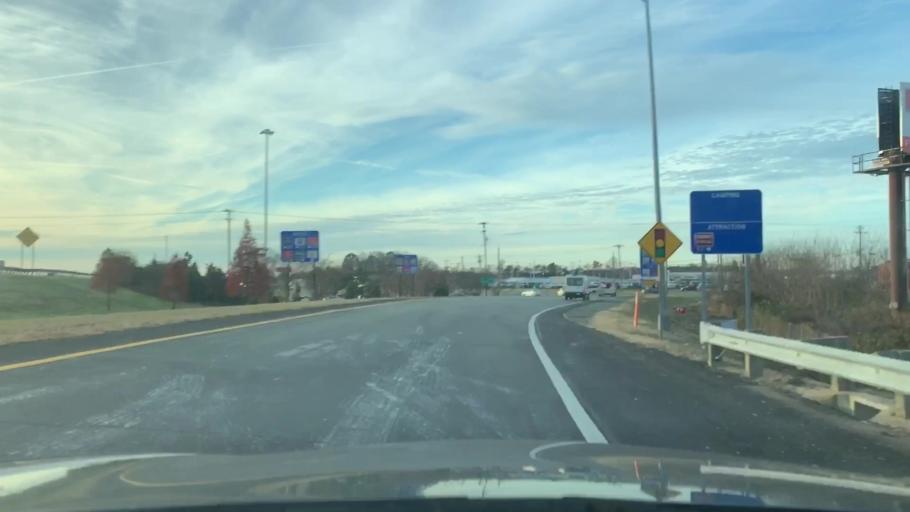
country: US
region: North Carolina
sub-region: Alamance County
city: Graham
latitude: 36.0640
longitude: -79.4292
